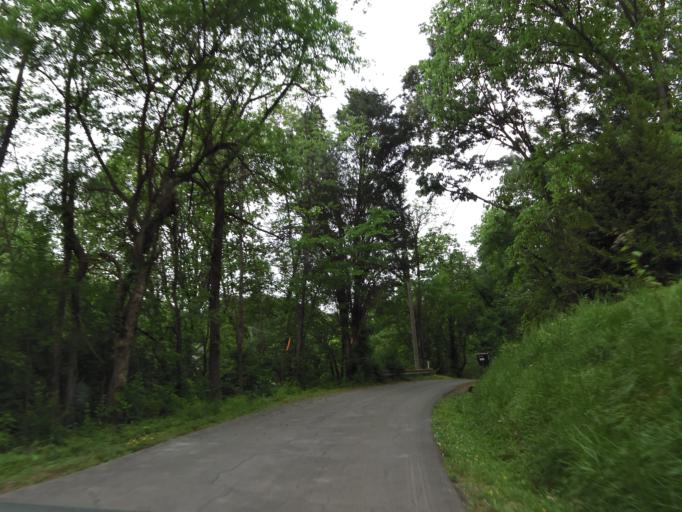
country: US
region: Tennessee
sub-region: Blount County
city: Eagleton Village
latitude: 35.7836
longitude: -83.9433
